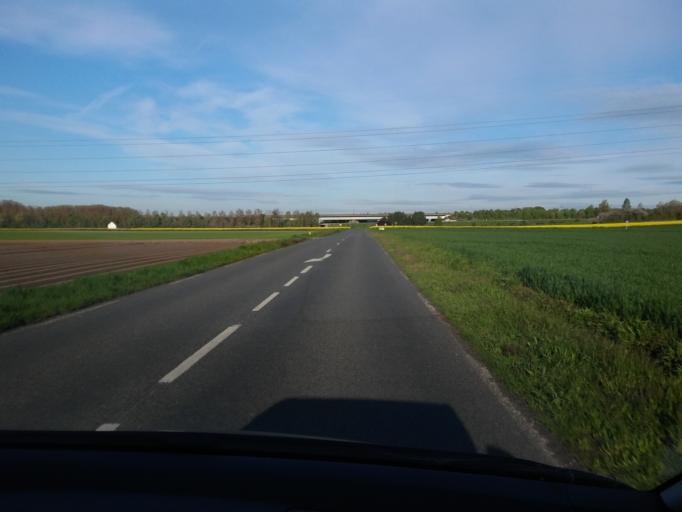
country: FR
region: Picardie
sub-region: Departement de l'Oise
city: Longueil-Sainte-Marie
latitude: 49.3493
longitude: 2.7101
